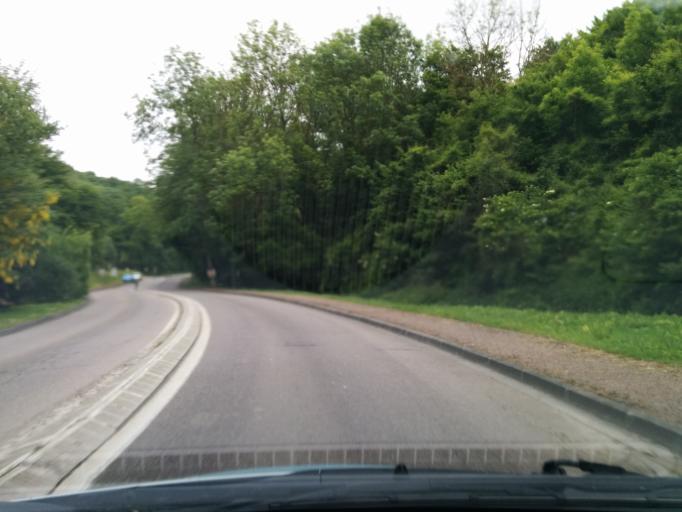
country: FR
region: Haute-Normandie
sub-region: Departement de l'Eure
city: Vernon
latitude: 49.1069
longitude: 1.4876
